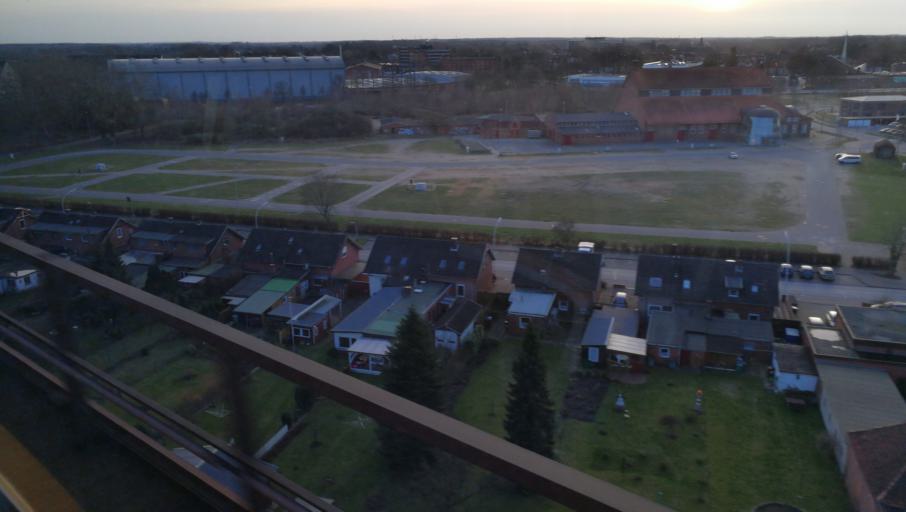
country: DE
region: Schleswig-Holstein
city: Rendsburg
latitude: 54.3013
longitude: 9.6800
